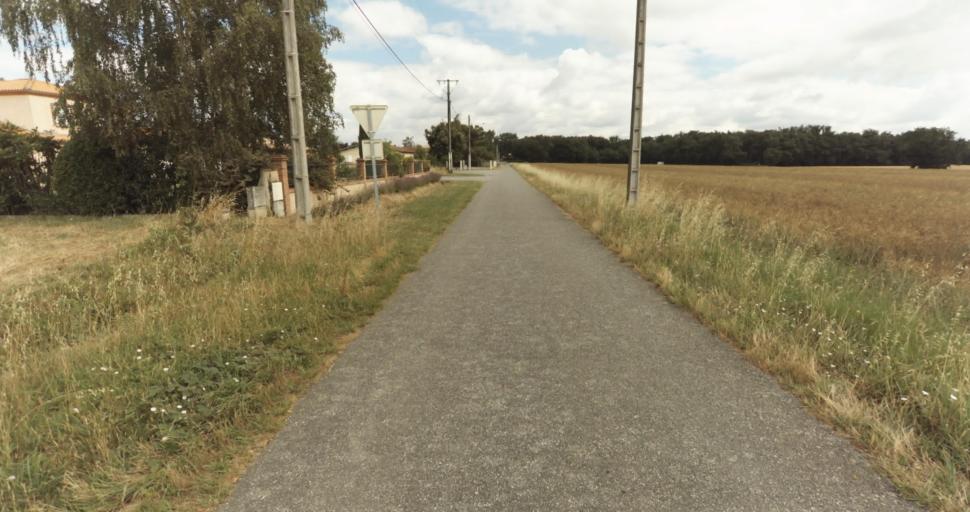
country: FR
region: Midi-Pyrenees
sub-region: Departement de la Haute-Garonne
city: Fontenilles
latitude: 43.5502
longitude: 1.2122
